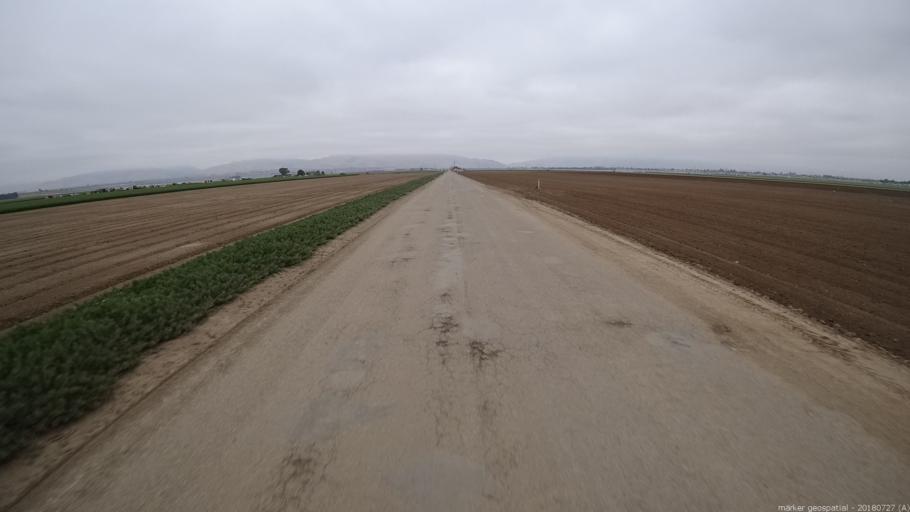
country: US
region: California
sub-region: Monterey County
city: Greenfield
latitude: 36.3222
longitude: -121.2044
